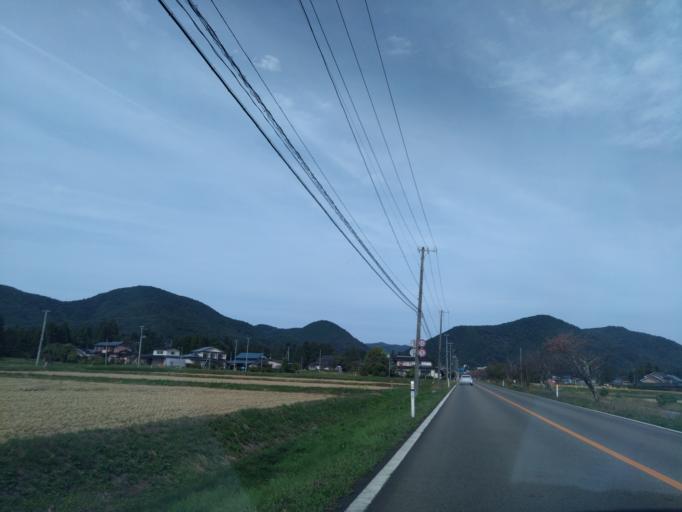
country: JP
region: Iwate
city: Hanamaki
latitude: 39.4403
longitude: 141.0778
